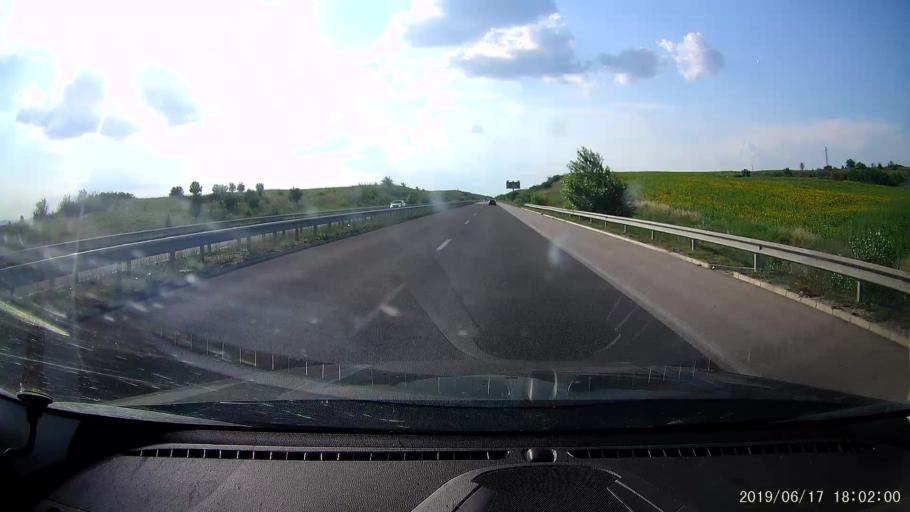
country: BG
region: Khaskovo
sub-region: Obshtina Svilengrad
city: Svilengrad
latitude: 41.7523
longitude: 26.2394
